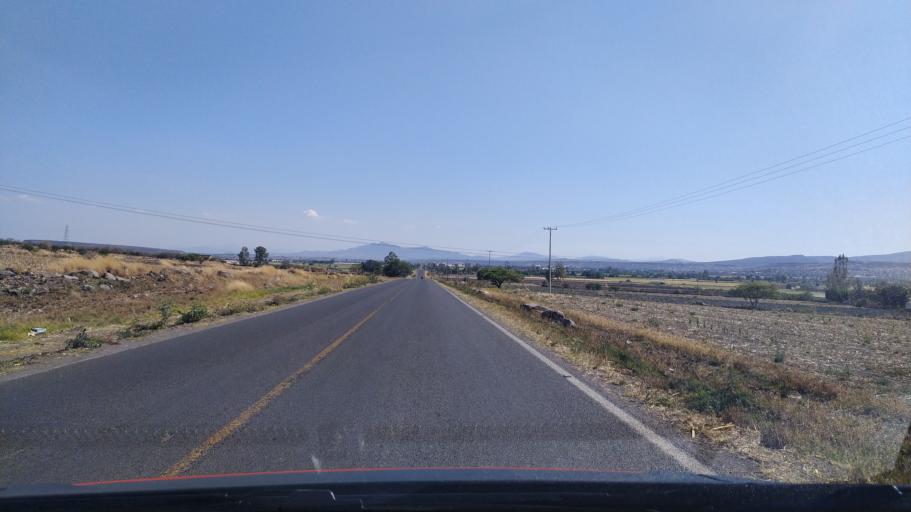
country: MX
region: Guanajuato
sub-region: Penjamo
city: Estacion la Piedad
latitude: 20.4074
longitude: -101.9983
